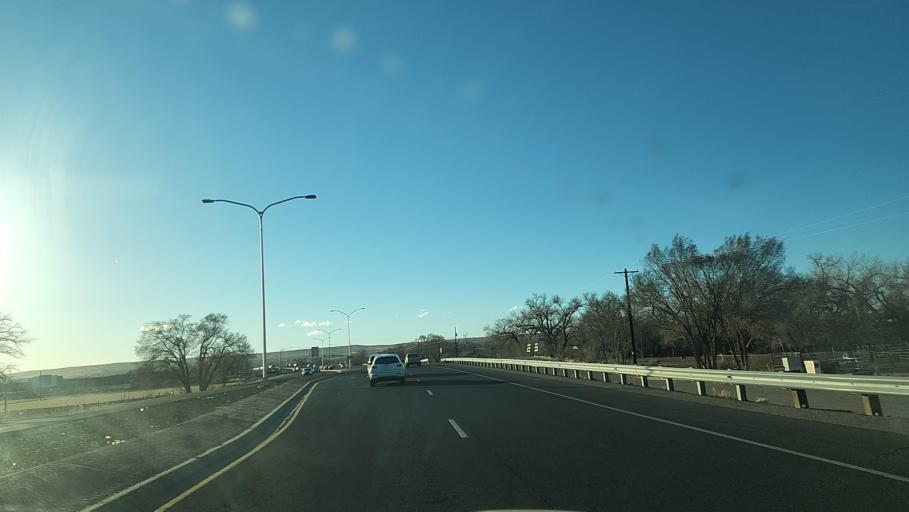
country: US
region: New Mexico
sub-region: Bernalillo County
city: South Valley
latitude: 35.0272
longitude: -106.7055
